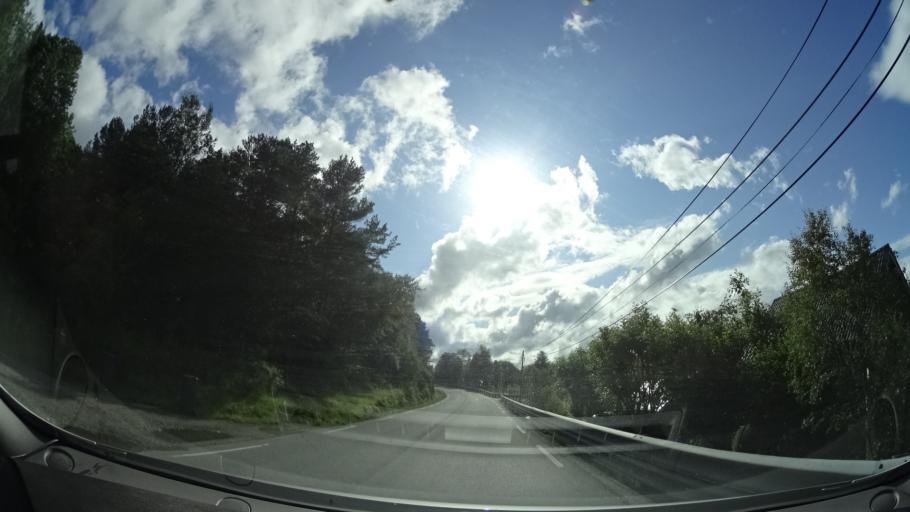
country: NO
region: More og Romsdal
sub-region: Halsa
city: Liaboen
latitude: 63.1344
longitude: 8.3976
